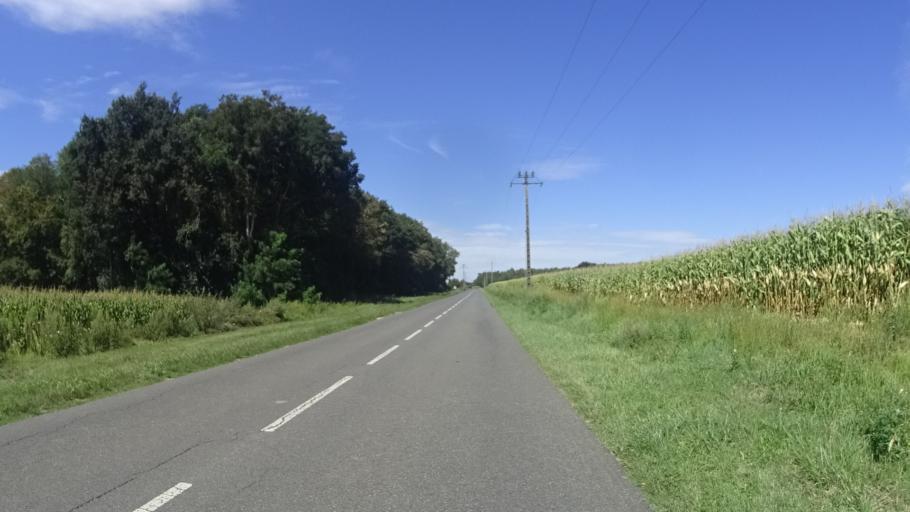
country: FR
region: Centre
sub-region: Departement du Loiret
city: Briare
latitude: 47.6129
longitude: 2.7575
